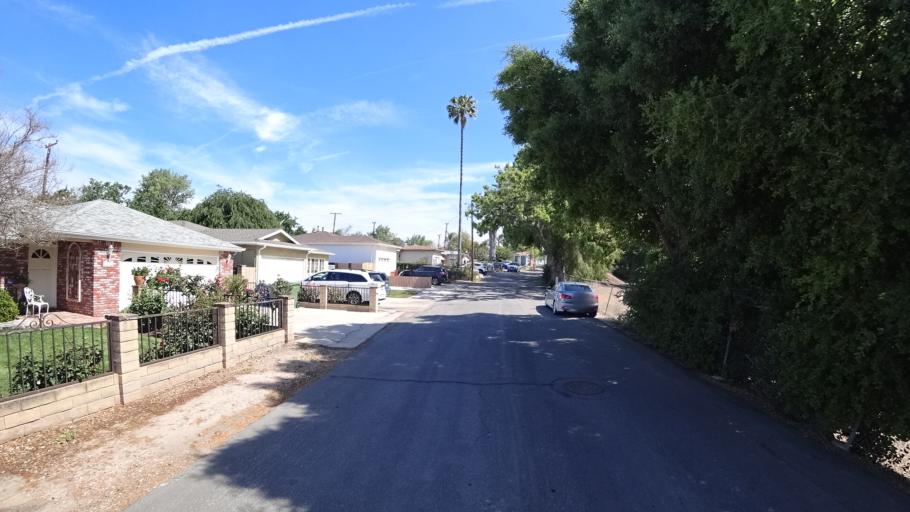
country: US
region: California
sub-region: Ventura County
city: Thousand Oaks
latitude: 34.1800
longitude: -118.8665
